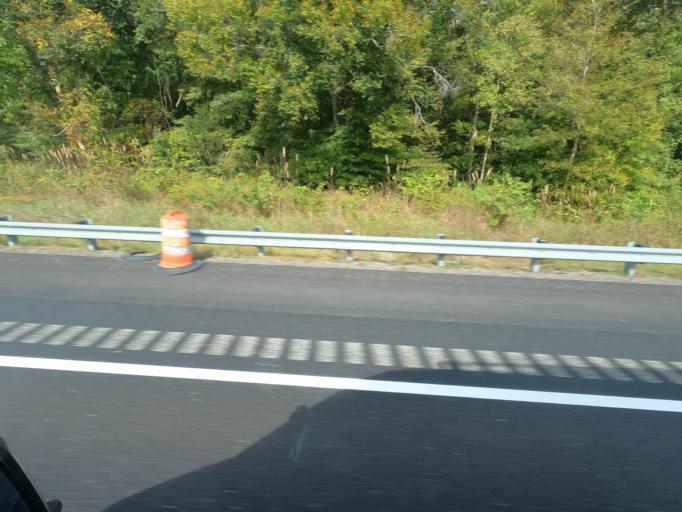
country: US
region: Tennessee
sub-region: Decatur County
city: Parsons
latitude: 35.8191
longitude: -88.1456
